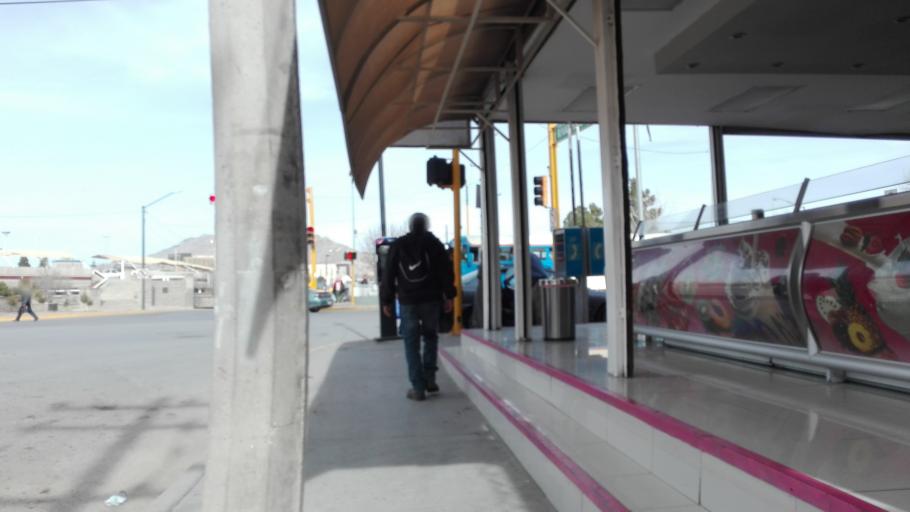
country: MX
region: Chihuahua
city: Ciudad Juarez
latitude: 31.7454
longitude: -106.4840
